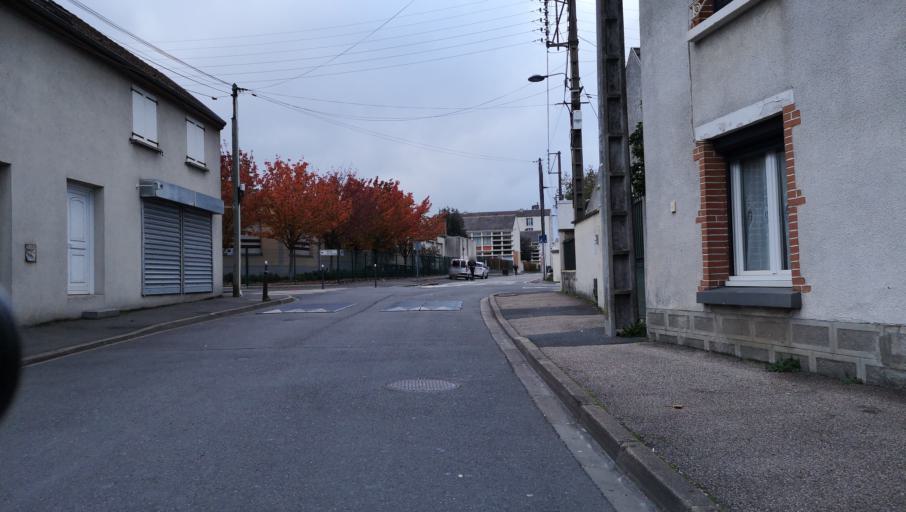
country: FR
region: Centre
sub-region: Departement du Loiret
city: Saint-Jean-le-Blanc
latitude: 47.9116
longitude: 1.9331
